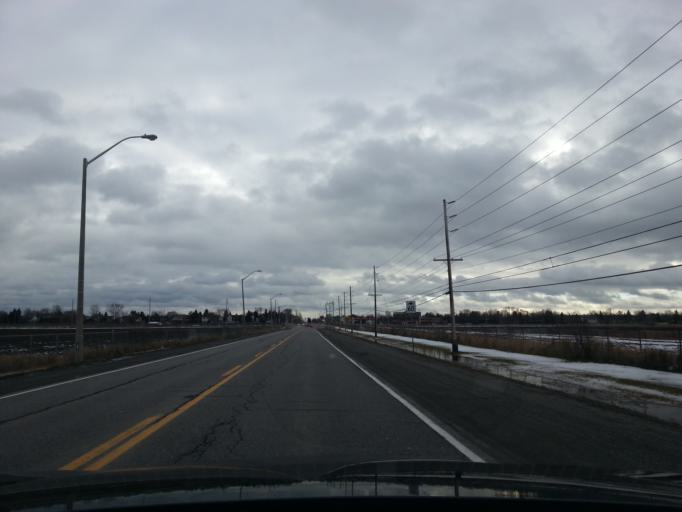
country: CA
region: Ontario
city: Bells Corners
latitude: 45.2919
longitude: -75.7594
